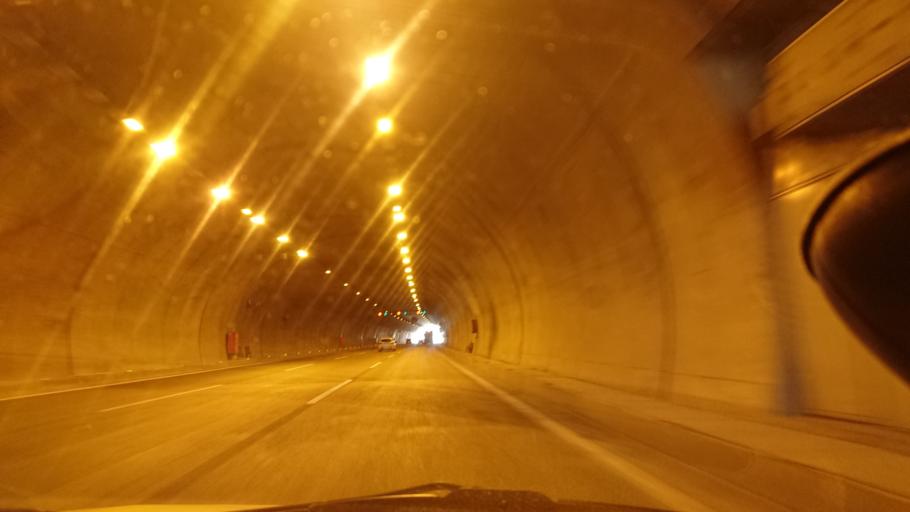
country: TR
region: Izmir
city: Karsiyaka
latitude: 38.4849
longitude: 27.1397
